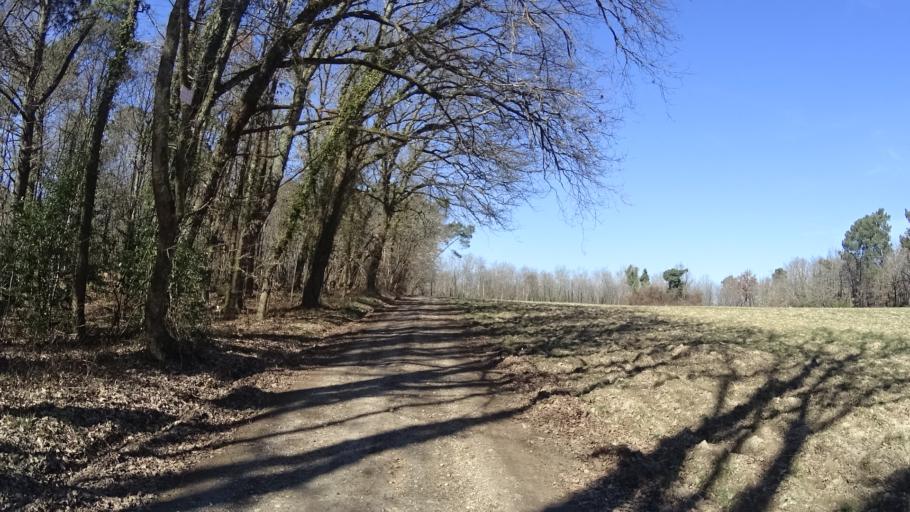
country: FR
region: Aquitaine
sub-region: Departement de la Dordogne
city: Riberac
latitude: 45.1905
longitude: 0.3082
